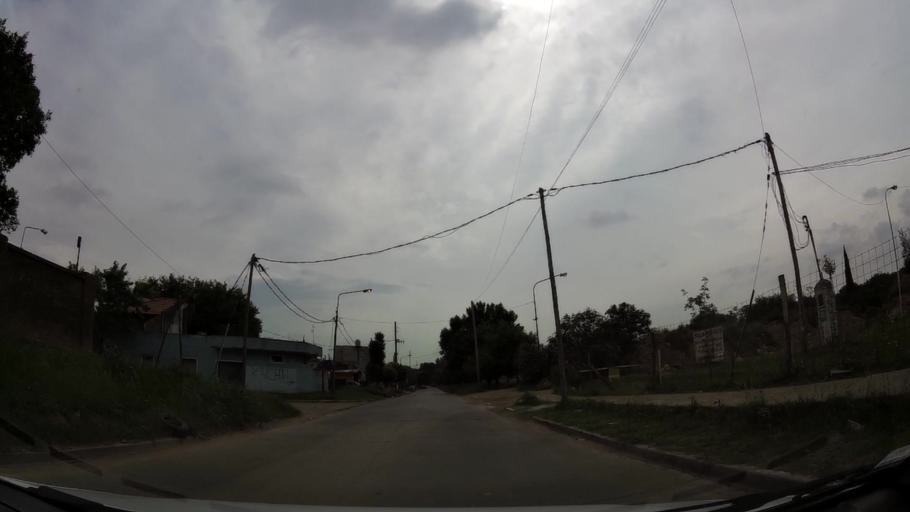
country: AR
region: Buenos Aires
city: San Justo
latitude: -34.6957
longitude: -58.5174
